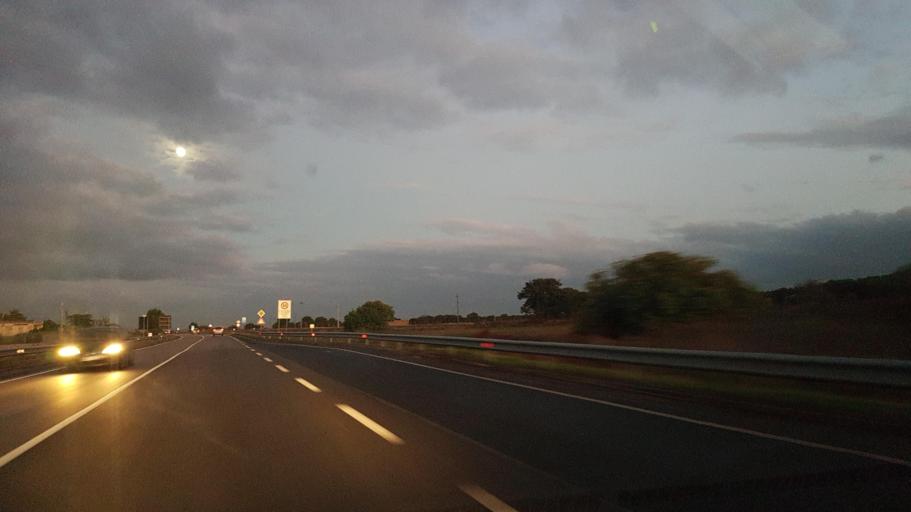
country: IT
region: Apulia
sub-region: Provincia di Taranto
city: Laterza
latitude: 40.6489
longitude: 16.8255
